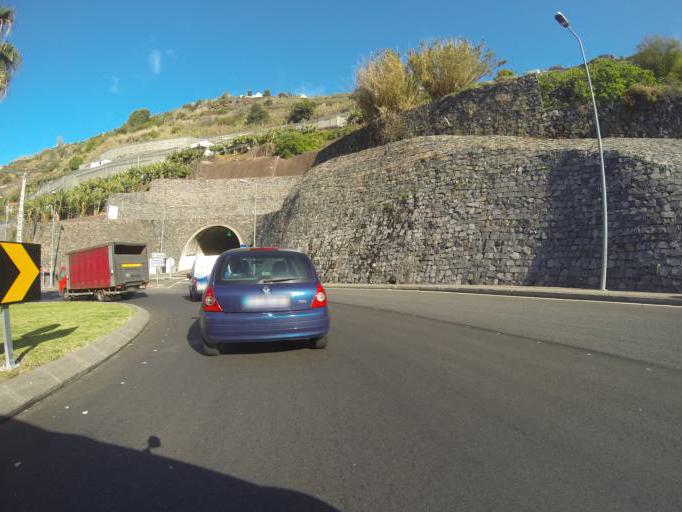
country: PT
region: Madeira
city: Calheta
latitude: 32.7273
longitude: -17.1745
